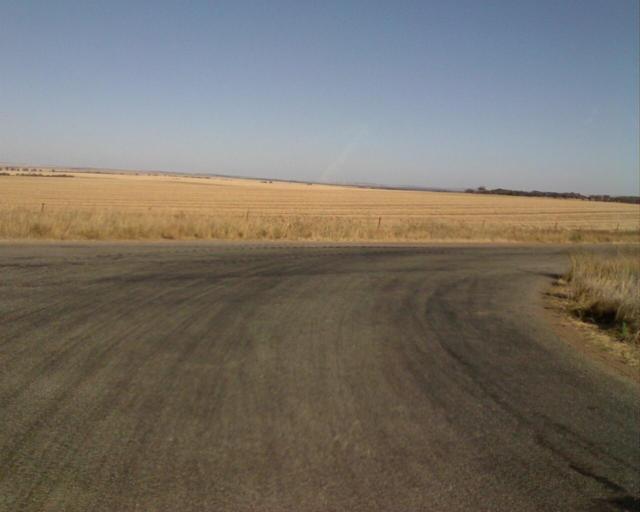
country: AU
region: Western Australia
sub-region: Moora
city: Moora
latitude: -30.2495
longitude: 116.3837
